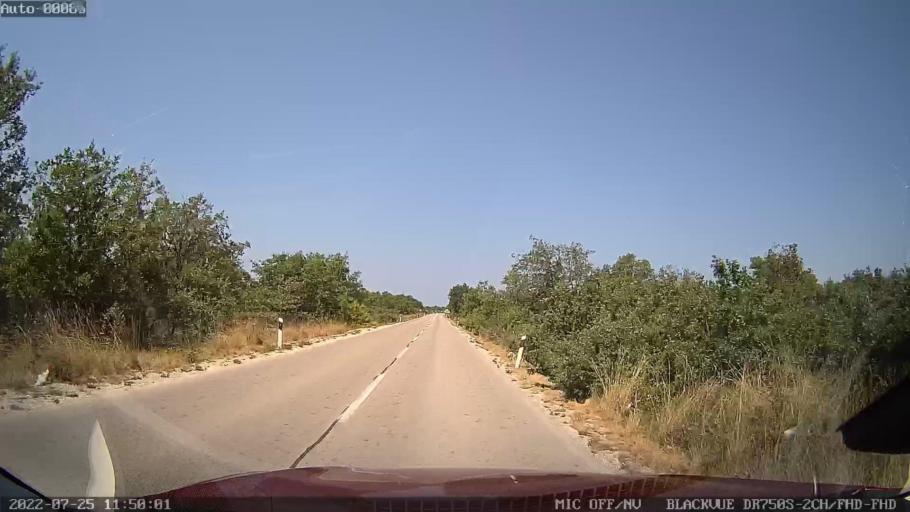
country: HR
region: Zadarska
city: Vrsi
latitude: 44.2357
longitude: 15.2719
